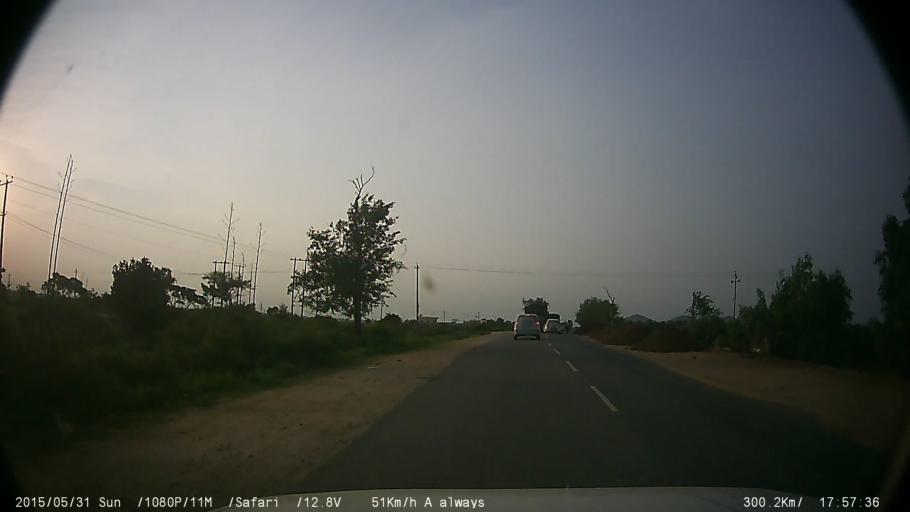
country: IN
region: Karnataka
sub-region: Mysore
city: Nanjangud
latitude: 12.0025
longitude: 76.6692
